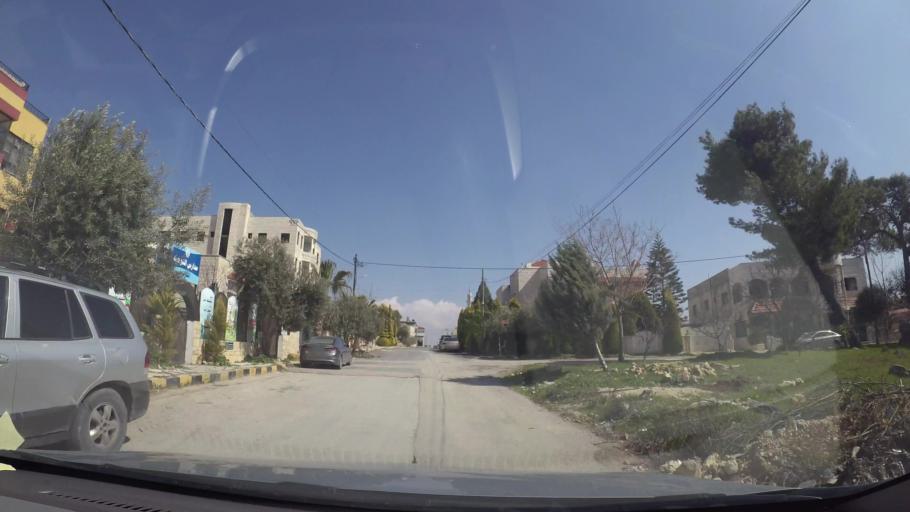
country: JO
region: Amman
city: Al Bunayyat ash Shamaliyah
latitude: 31.9041
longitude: 35.8969
